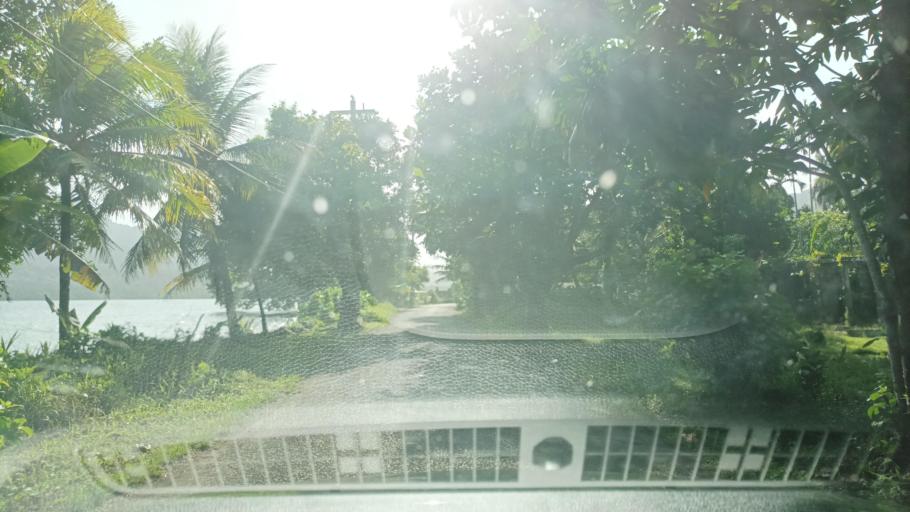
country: FM
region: Kosrae
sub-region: Lelu Municipality
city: Lelu
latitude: 5.3287
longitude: 163.0280
